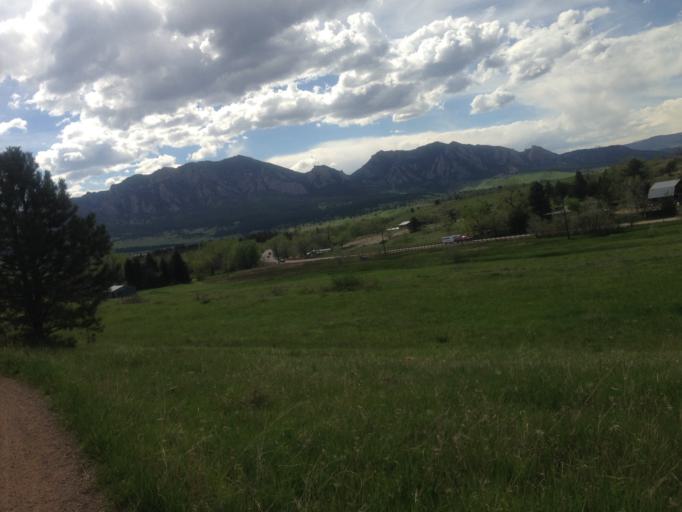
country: US
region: Colorado
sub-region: Boulder County
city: Superior
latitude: 39.9543
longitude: -105.2182
